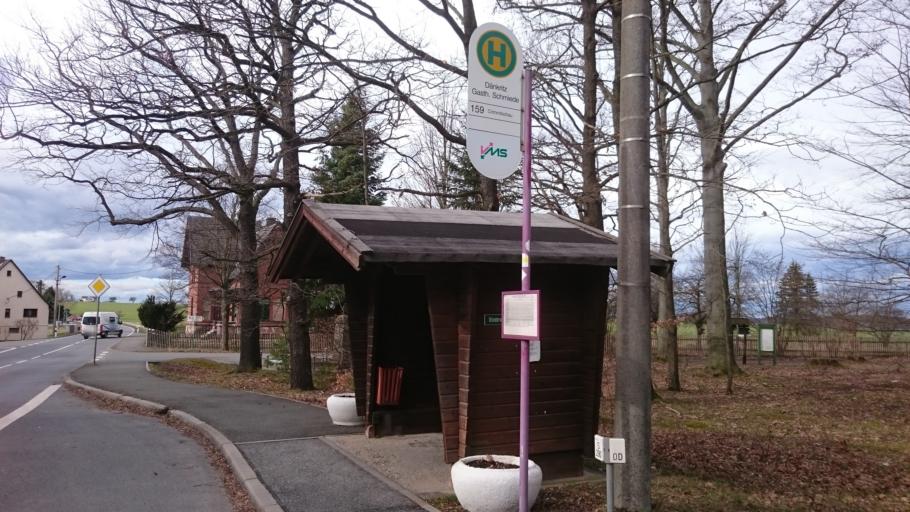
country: DE
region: Saxony
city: Hartmannsdorf
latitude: 50.7769
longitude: 12.4282
